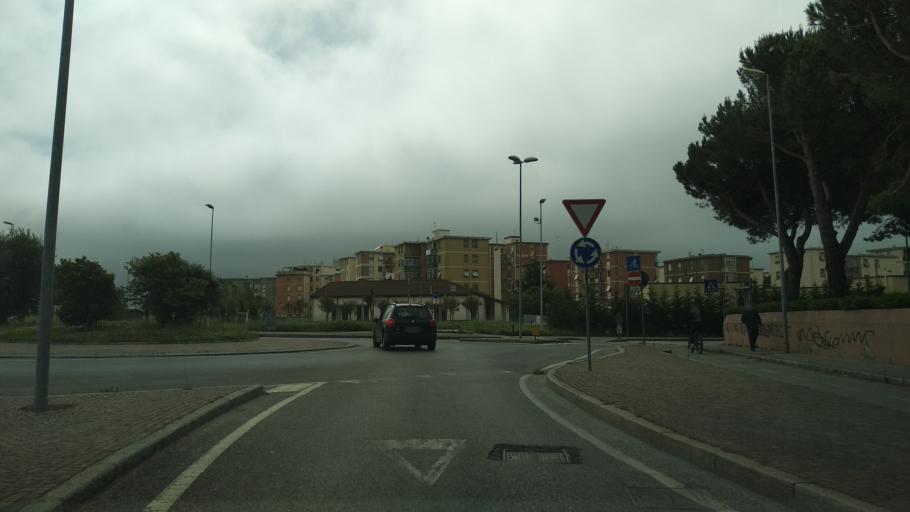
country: IT
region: Tuscany
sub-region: Provincia di Livorno
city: Livorno
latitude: 43.5403
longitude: 10.3303
